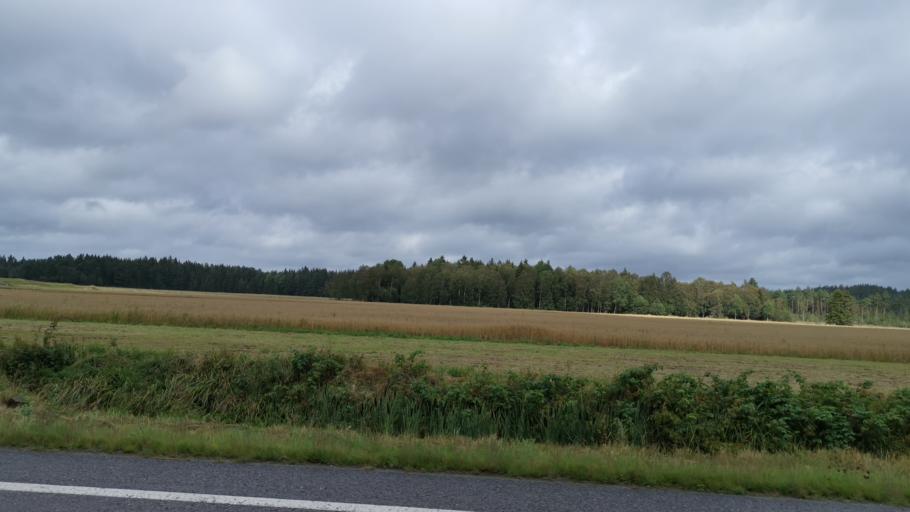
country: SE
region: Vaestra Goetaland
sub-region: Uddevalla Kommun
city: Uddevalla
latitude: 58.3442
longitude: 12.0469
